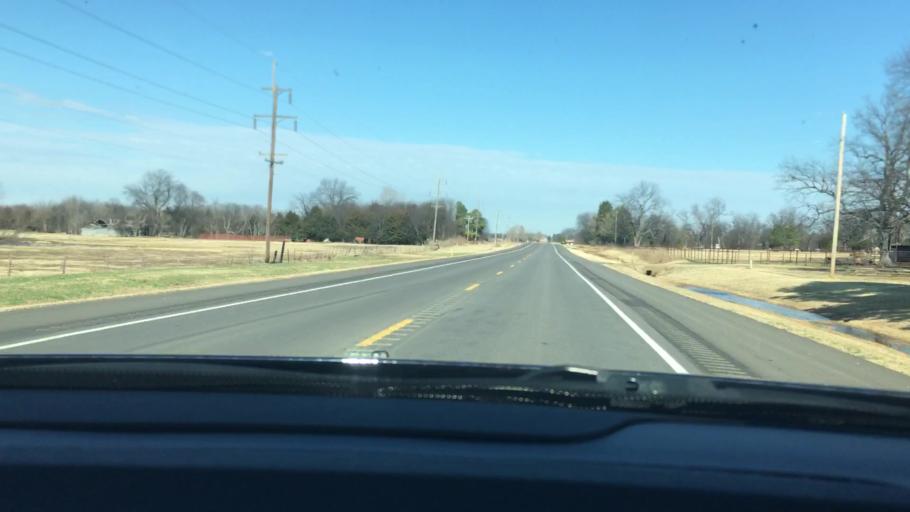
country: US
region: Oklahoma
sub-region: Garvin County
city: Wynnewood
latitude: 34.5840
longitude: -97.1425
